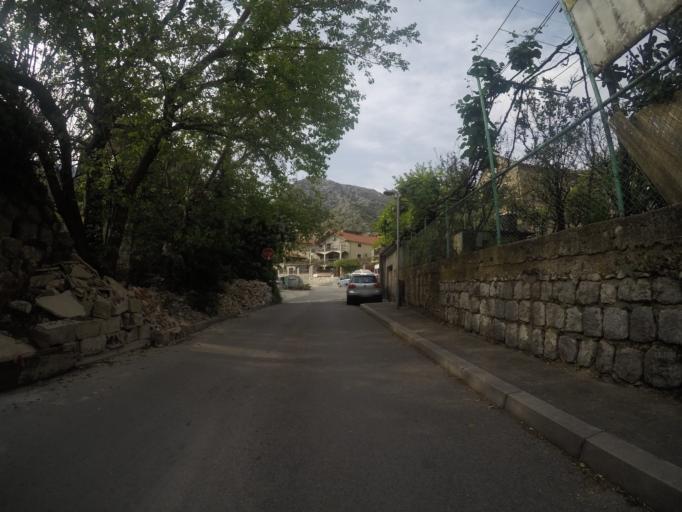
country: ME
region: Kotor
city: Risan
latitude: 42.5134
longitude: 18.6959
